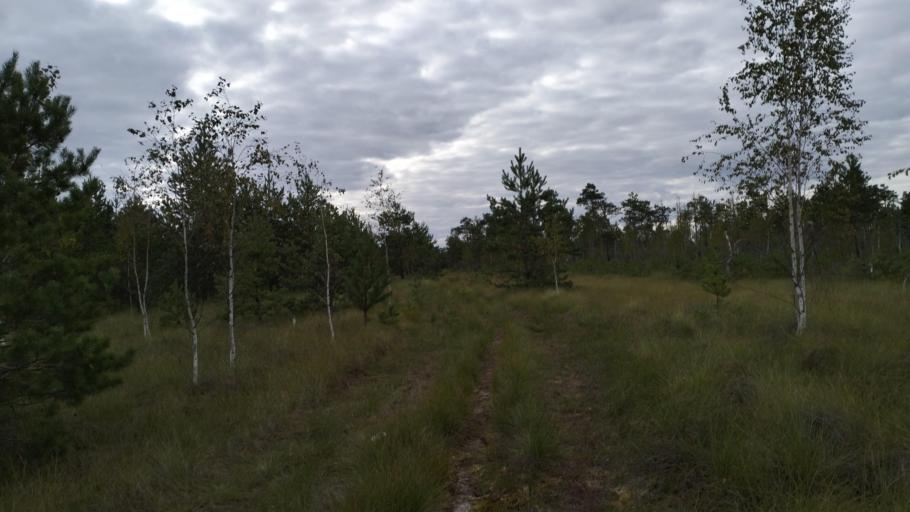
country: BY
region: Brest
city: Davyd-Haradok
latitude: 51.8959
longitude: 27.2123
